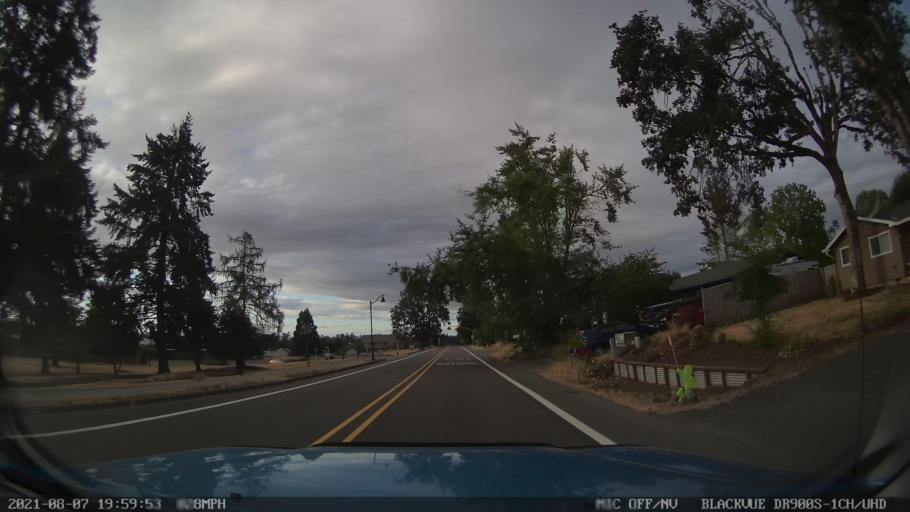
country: US
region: Oregon
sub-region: Marion County
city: Silverton
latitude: 45.0001
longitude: -122.7923
